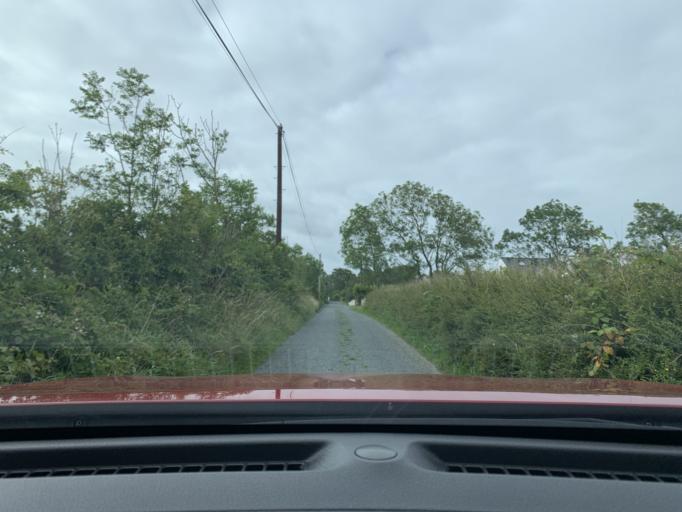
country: IE
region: Connaught
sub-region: Sligo
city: Sligo
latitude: 54.3866
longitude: -8.5224
